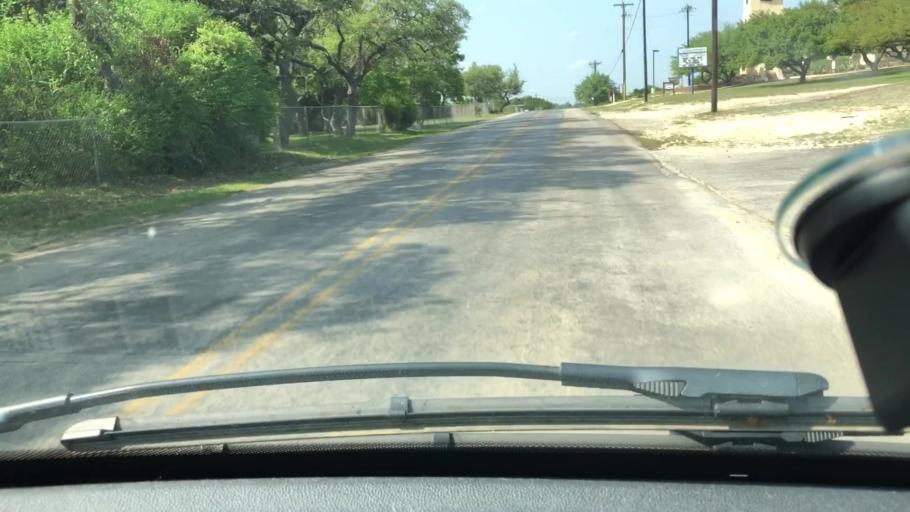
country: US
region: Texas
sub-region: Comal County
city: Bulverde
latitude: 29.7674
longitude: -98.4588
